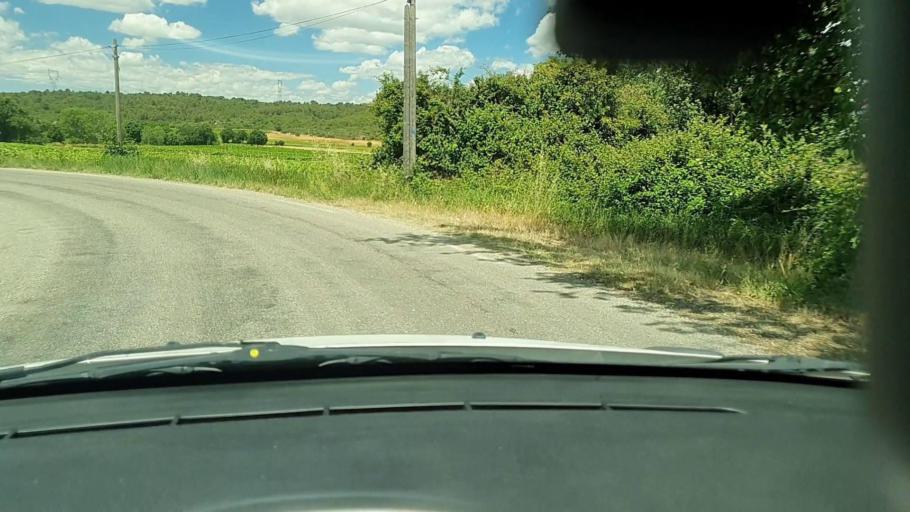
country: FR
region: Languedoc-Roussillon
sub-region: Departement du Gard
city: Poulx
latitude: 43.9518
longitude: 4.4172
